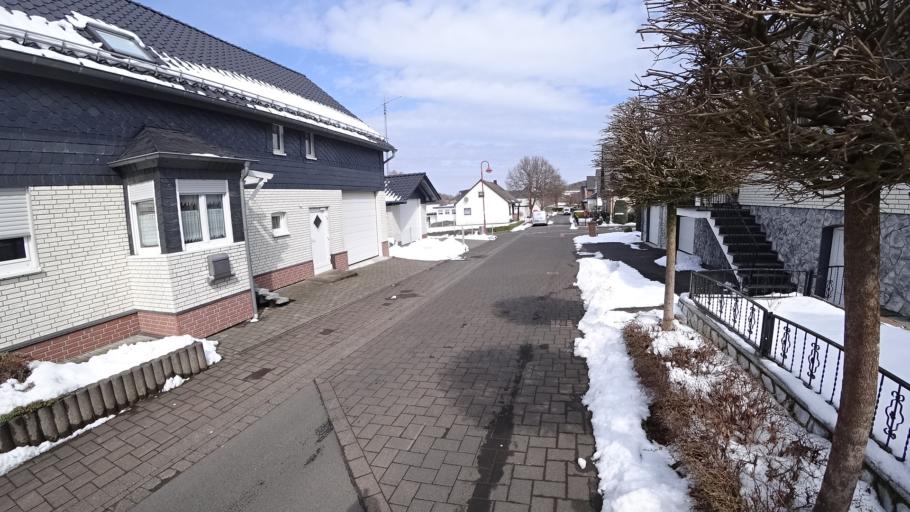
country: DE
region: Rheinland-Pfalz
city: Elkenroth
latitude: 50.7270
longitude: 7.8848
